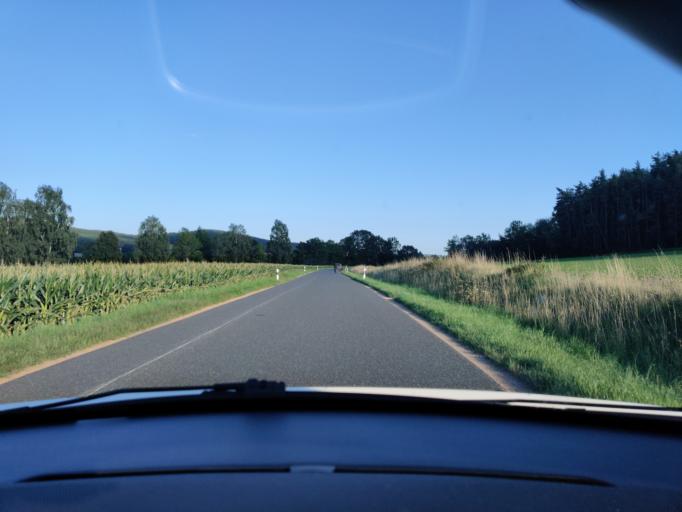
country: DE
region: Bavaria
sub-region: Upper Palatinate
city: Stulln
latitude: 49.4161
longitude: 12.1570
